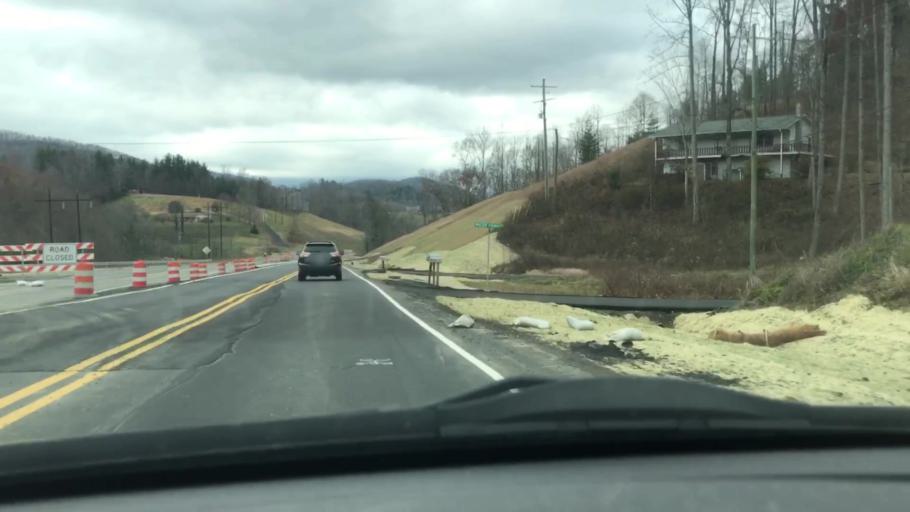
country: US
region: North Carolina
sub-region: Mitchell County
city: Spruce Pine
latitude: 35.9041
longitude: -82.1099
